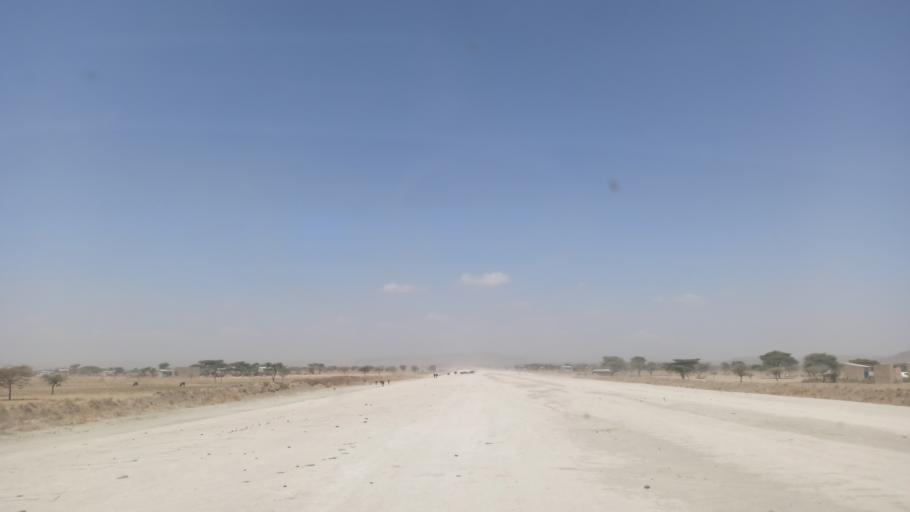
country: ET
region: Oromiya
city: Ziway
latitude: 7.7238
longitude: 38.6292
